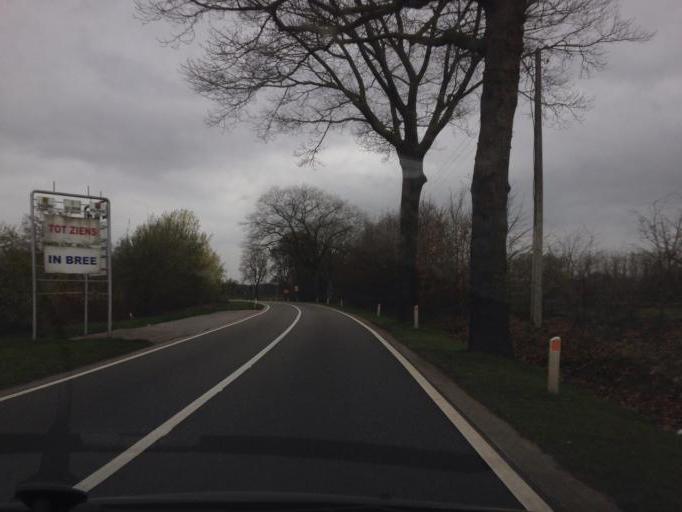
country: BE
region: Flanders
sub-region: Provincie Limburg
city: Bree
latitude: 51.1223
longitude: 5.5569
